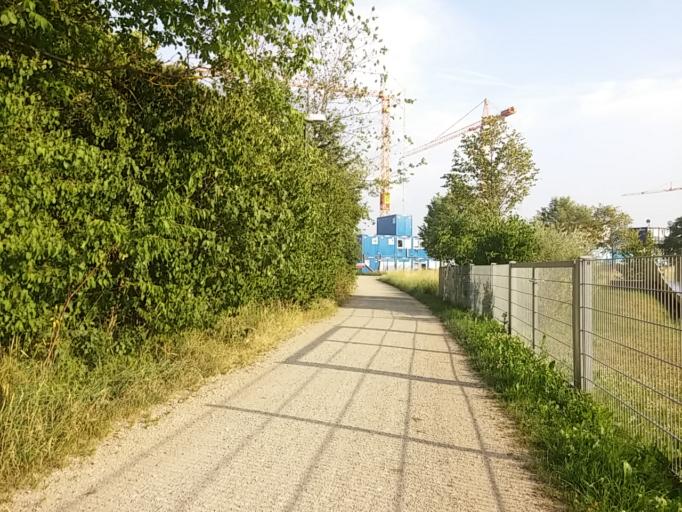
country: DE
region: Bavaria
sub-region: Upper Bavaria
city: Vaterstetten
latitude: 48.1130
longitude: 11.7688
